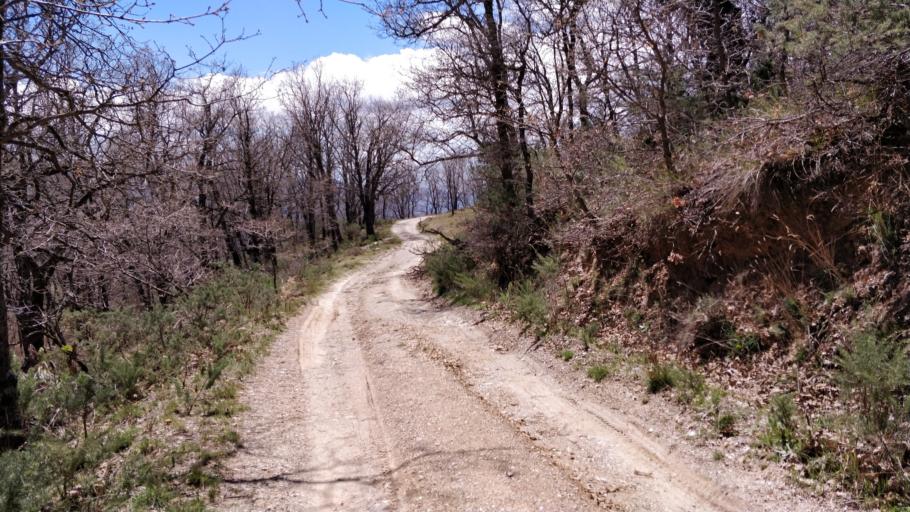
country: ES
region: Andalusia
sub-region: Provincia de Granada
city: Soportujar
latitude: 36.9434
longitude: -3.3894
